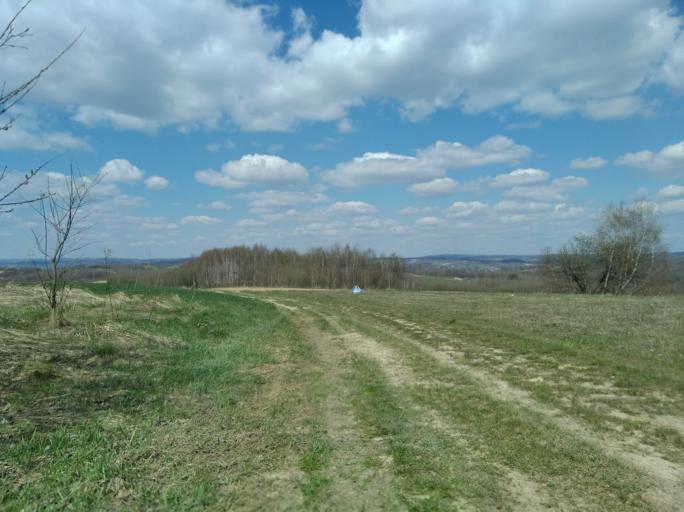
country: PL
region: Subcarpathian Voivodeship
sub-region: Powiat strzyzowski
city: Wysoka Strzyzowska
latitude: 49.8410
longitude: 21.7627
